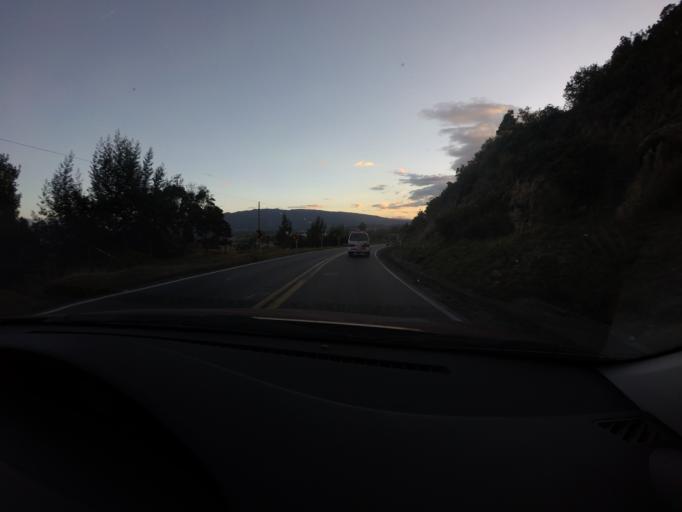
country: CO
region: Cundinamarca
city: Nemocon
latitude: 5.1156
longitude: -73.9074
